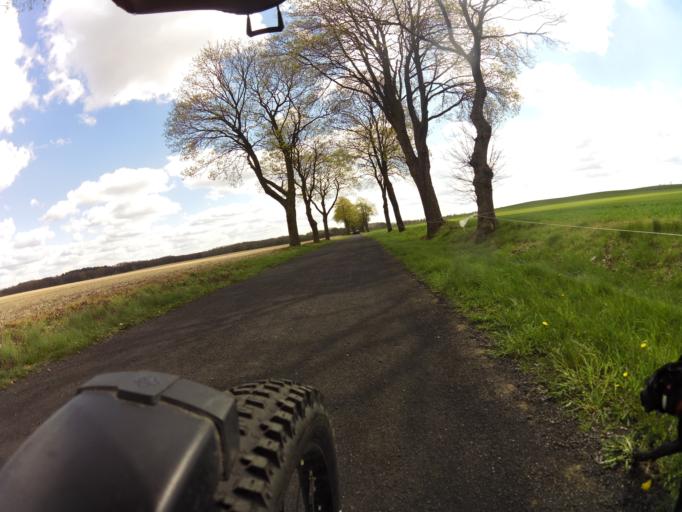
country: PL
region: West Pomeranian Voivodeship
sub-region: Powiat gryficki
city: Gryfice
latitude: 53.8545
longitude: 15.1674
